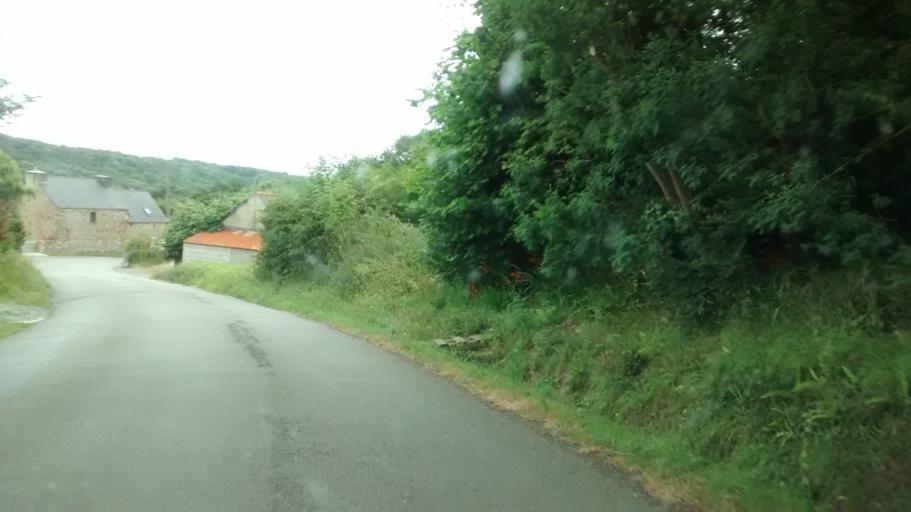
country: FR
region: Brittany
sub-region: Departement du Finistere
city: Plougastel-Daoulas
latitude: 48.3519
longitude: -4.3905
